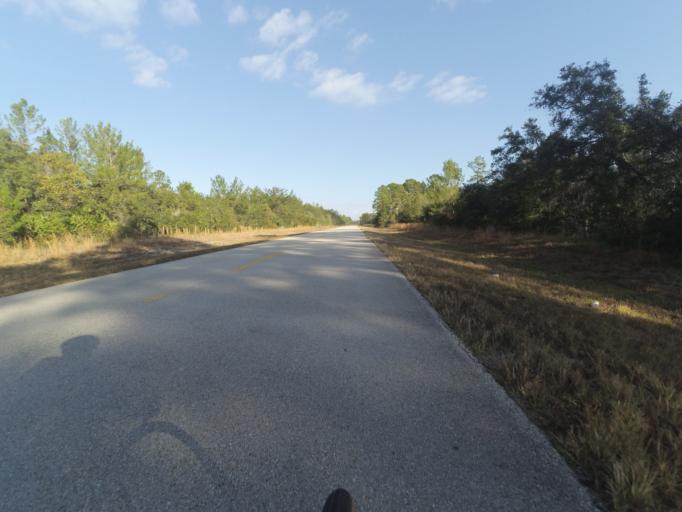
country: US
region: Florida
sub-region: Lake County
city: Astor
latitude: 29.1391
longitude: -81.5758
